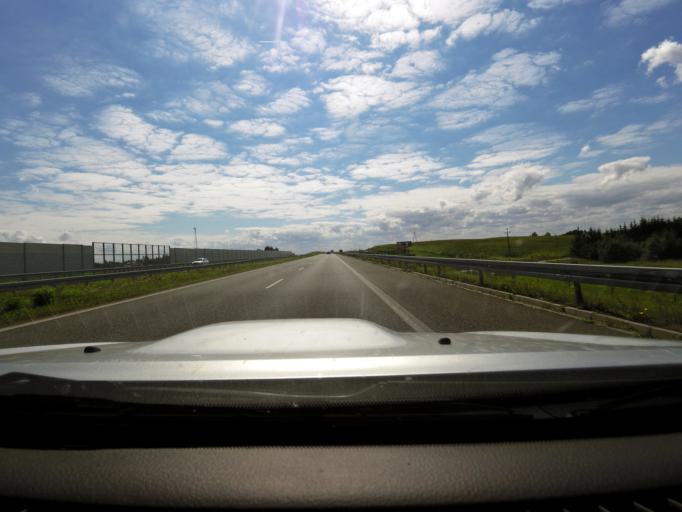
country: PL
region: Warmian-Masurian Voivodeship
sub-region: Powiat ostrodzki
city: Milomlyn
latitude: 53.8176
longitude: 19.7797
